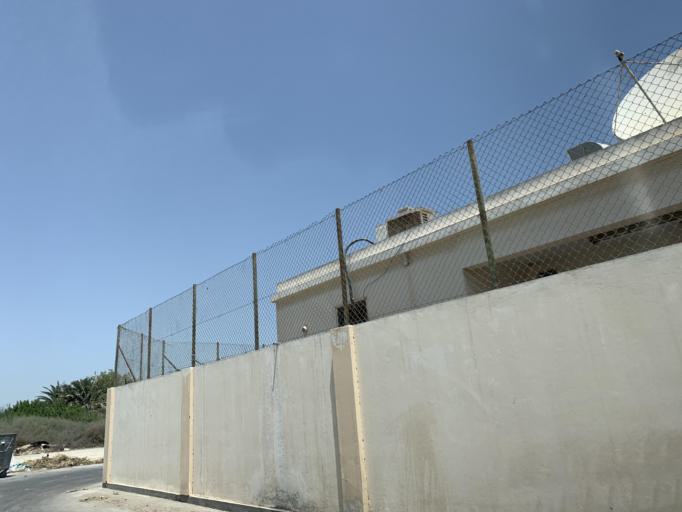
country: BH
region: Manama
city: Jidd Hafs
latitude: 26.2252
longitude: 50.4757
